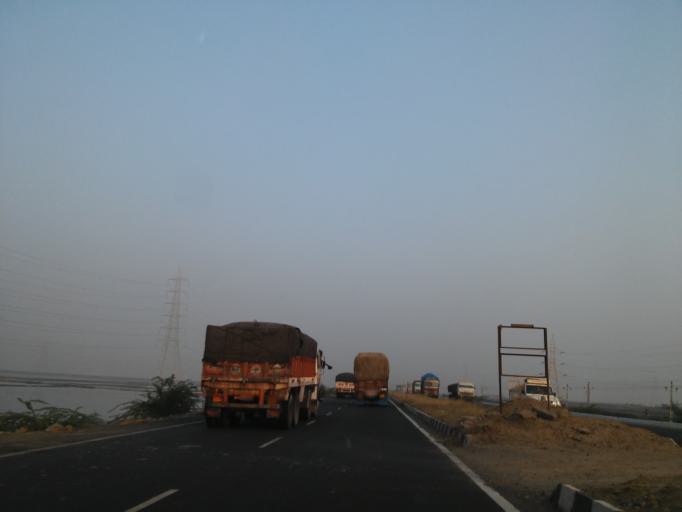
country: IN
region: Gujarat
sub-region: Rajkot
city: Morbi
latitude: 23.1539
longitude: 70.7395
